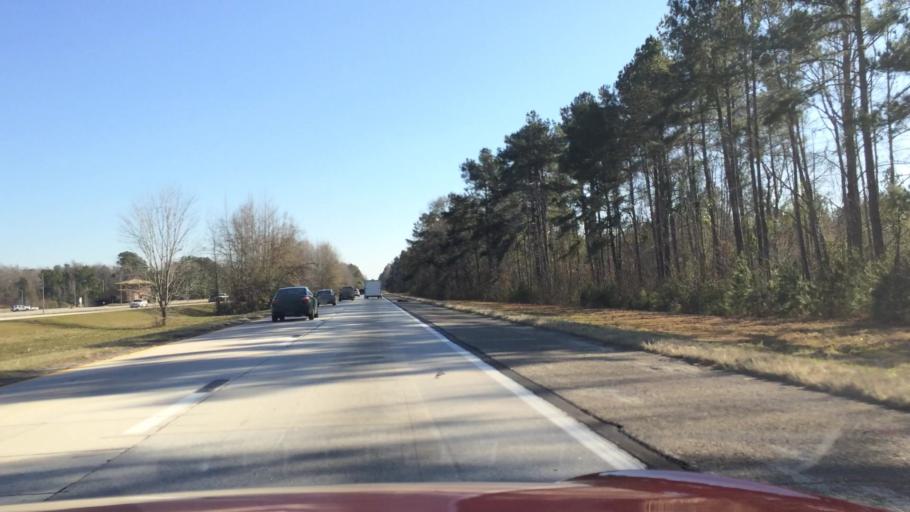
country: US
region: South Carolina
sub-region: Orangeburg County
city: Holly Hill
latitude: 33.2621
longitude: -80.4786
